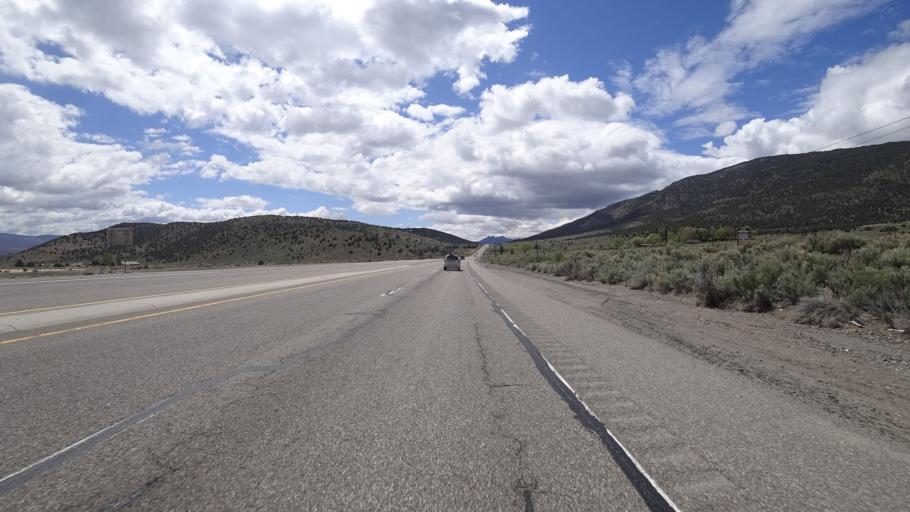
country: US
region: Nevada
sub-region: Lyon County
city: Smith Valley
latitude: 38.7276
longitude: -119.5553
